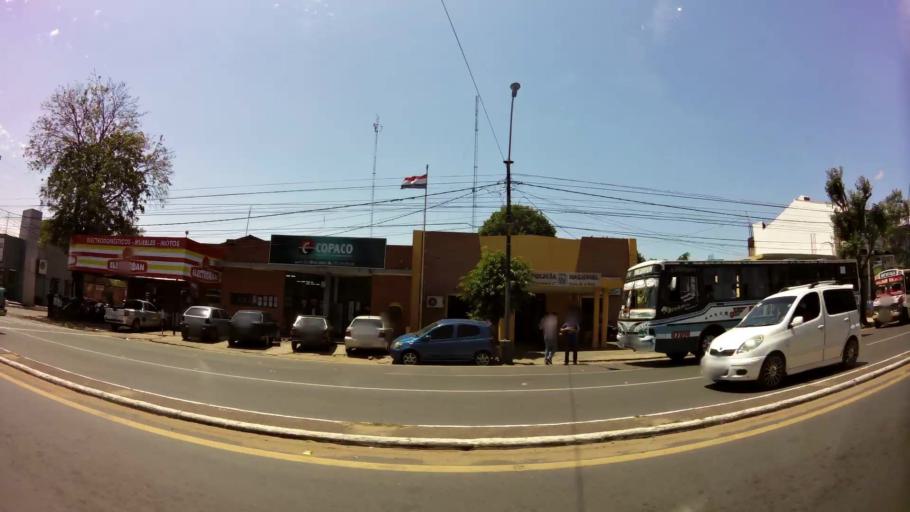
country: PY
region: Central
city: Fernando de la Mora
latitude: -25.3223
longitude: -57.5557
